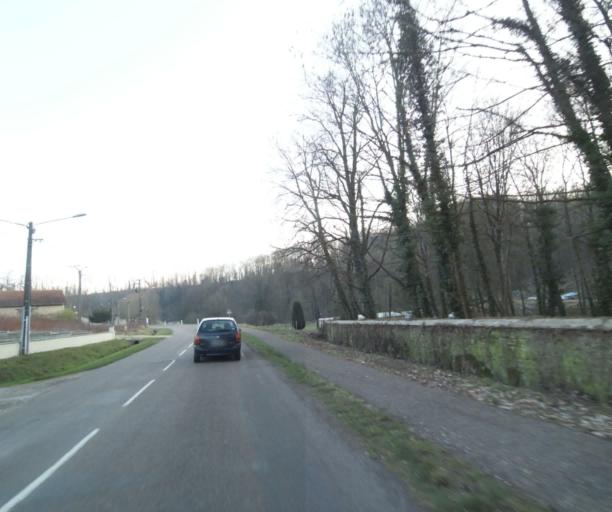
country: FR
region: Champagne-Ardenne
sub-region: Departement de la Haute-Marne
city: Bienville
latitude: 48.6096
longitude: 5.0512
